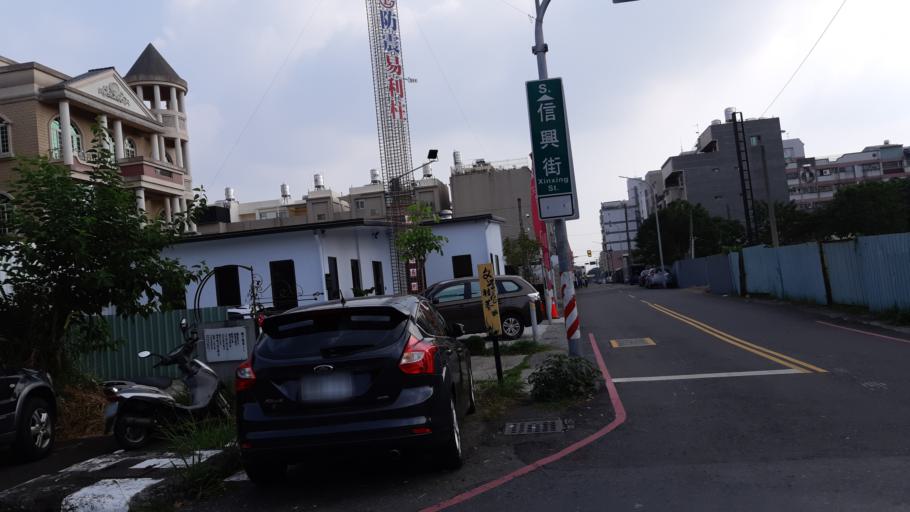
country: TW
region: Taiwan
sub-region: Chiayi
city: Jiayi Shi
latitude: 23.4683
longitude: 120.4588
